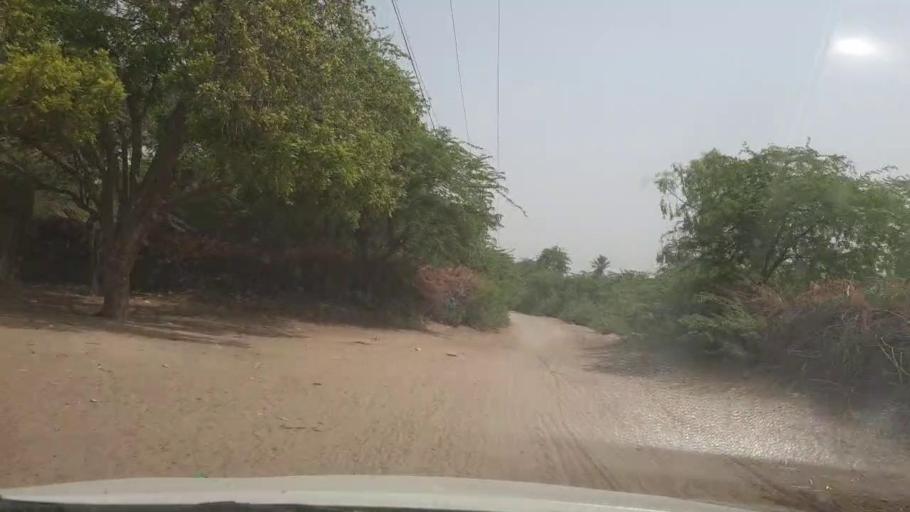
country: PK
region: Sindh
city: Kot Diji
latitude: 27.3460
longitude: 68.7171
